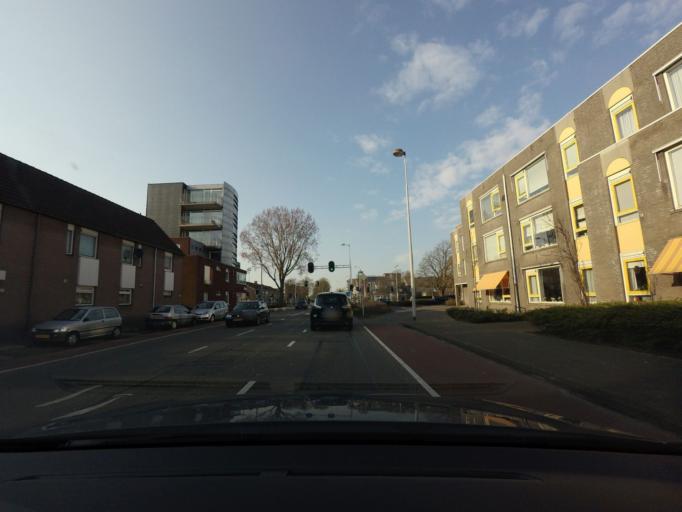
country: NL
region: North Holland
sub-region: Gemeente Beverwijk
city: Beverwijk
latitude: 52.4929
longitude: 4.6595
